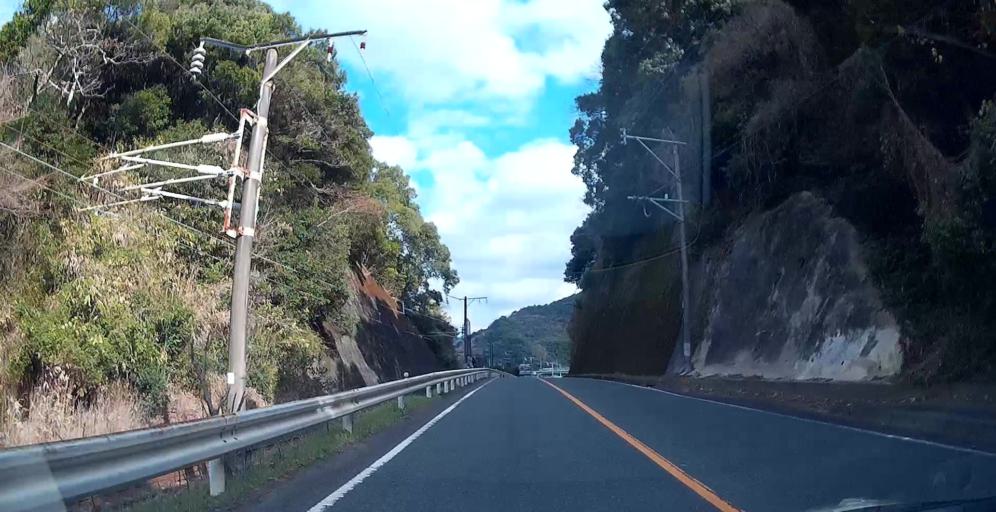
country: JP
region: Kumamoto
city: Yatsushiro
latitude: 32.4260
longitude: 130.5599
